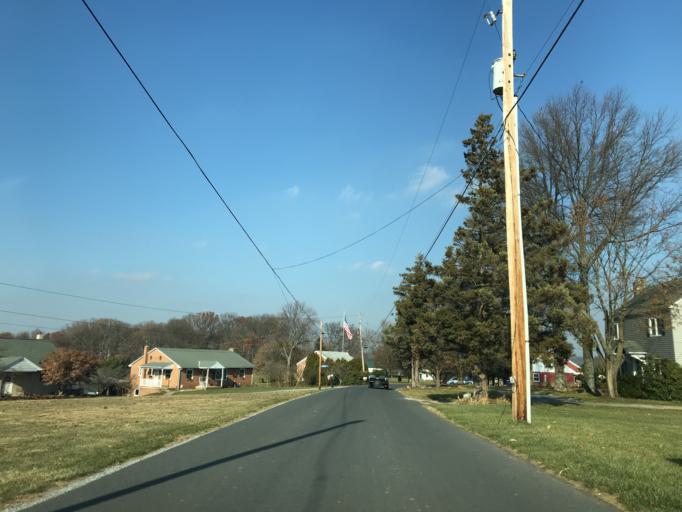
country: US
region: Pennsylvania
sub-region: York County
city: Jacobus
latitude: 39.8756
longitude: -76.6922
